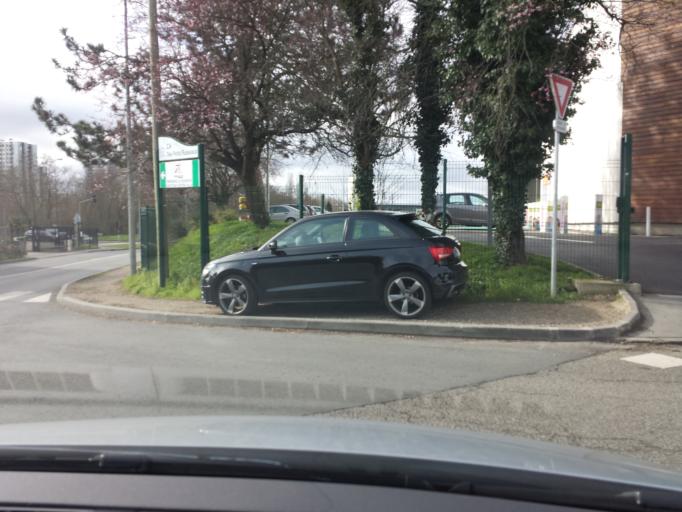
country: FR
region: Ile-de-France
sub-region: Departement de l'Essonne
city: Verrieres-le-Buisson
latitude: 48.7459
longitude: 2.2838
